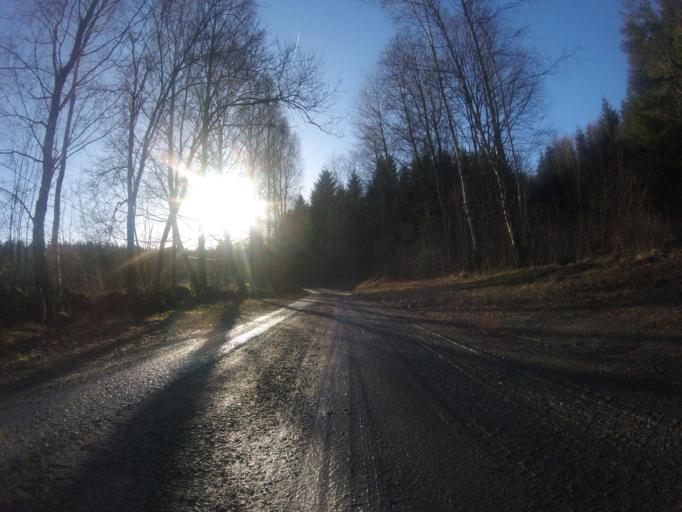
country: SE
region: Halland
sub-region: Varbergs Kommun
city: Veddige
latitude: 57.2261
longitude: 12.2973
